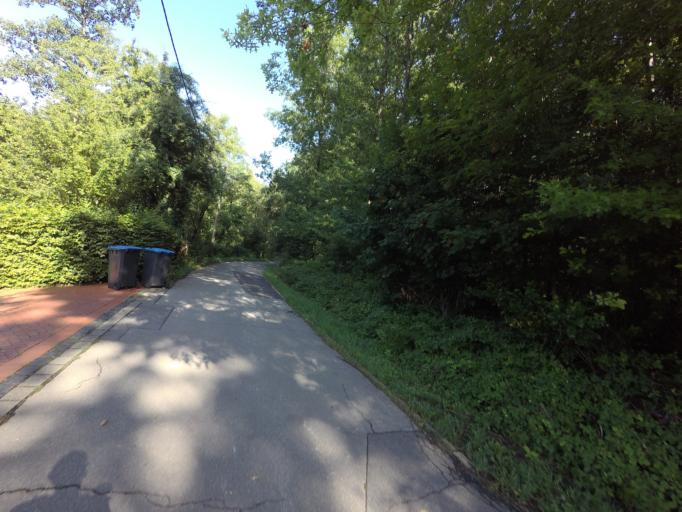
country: DE
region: North Rhine-Westphalia
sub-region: Regierungsbezirk Koln
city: Herzogenrath
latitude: 50.8451
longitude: 6.0971
